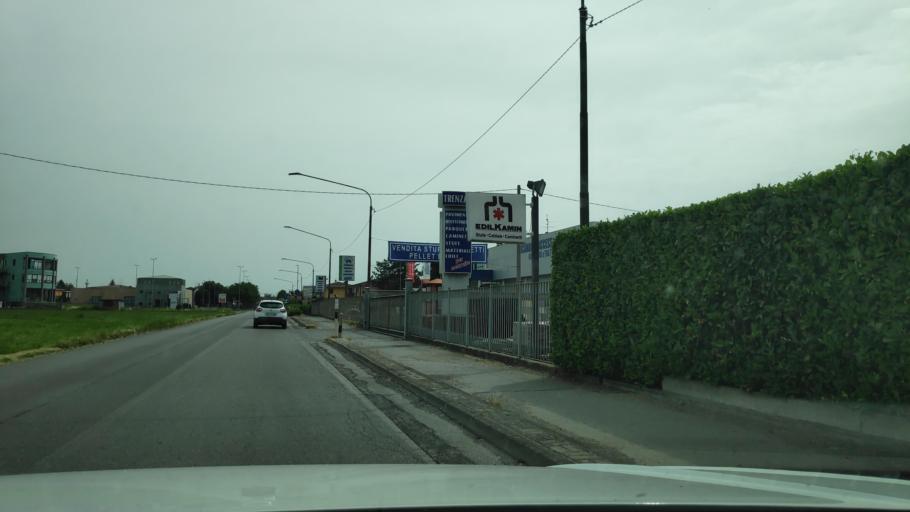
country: IT
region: Lombardy
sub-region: Provincia di Brescia
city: Orzinuovi
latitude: 45.4117
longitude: 9.9272
